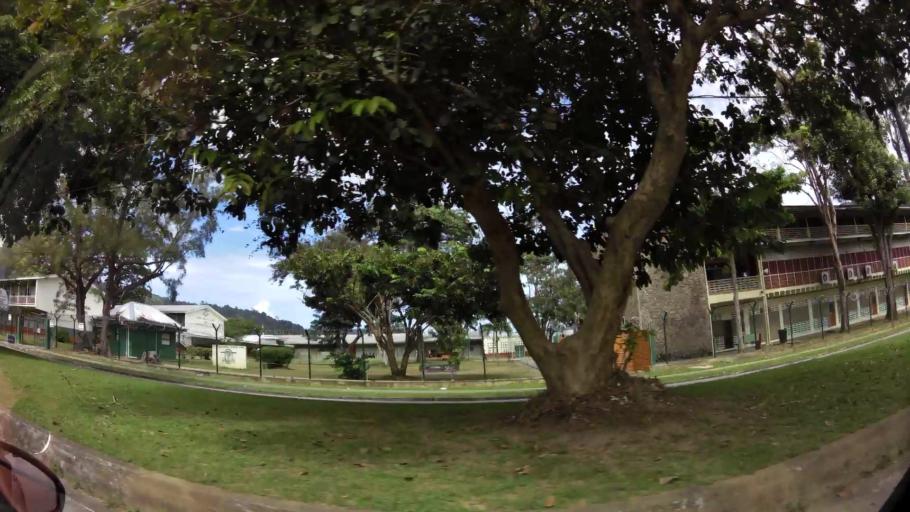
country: TT
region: Diego Martin
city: Petit Valley
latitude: 10.7180
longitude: -61.5594
